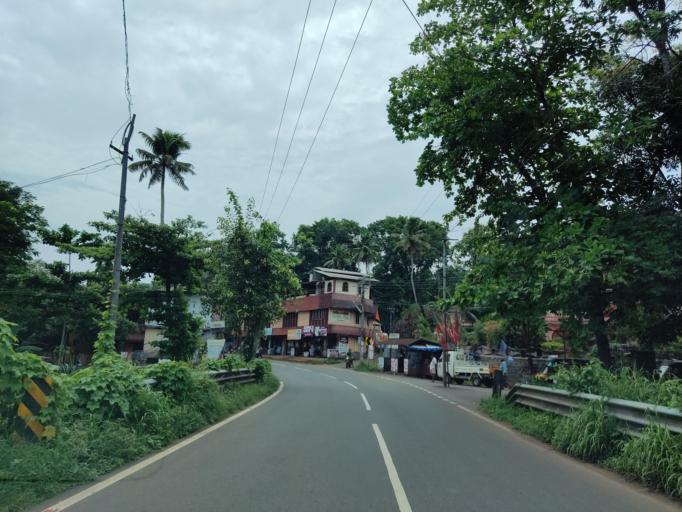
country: IN
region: Kerala
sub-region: Alappuzha
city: Chengannur
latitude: 9.2822
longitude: 76.6148
